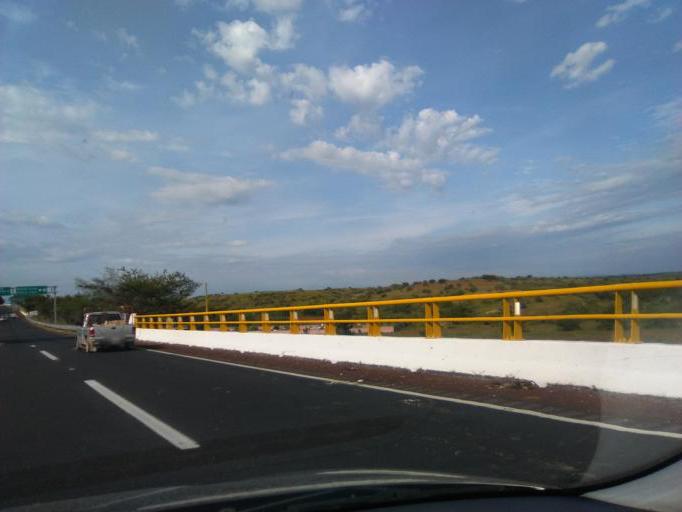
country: MX
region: Morelos
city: Ahuehuetzingo
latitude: 18.6500
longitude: -99.2953
